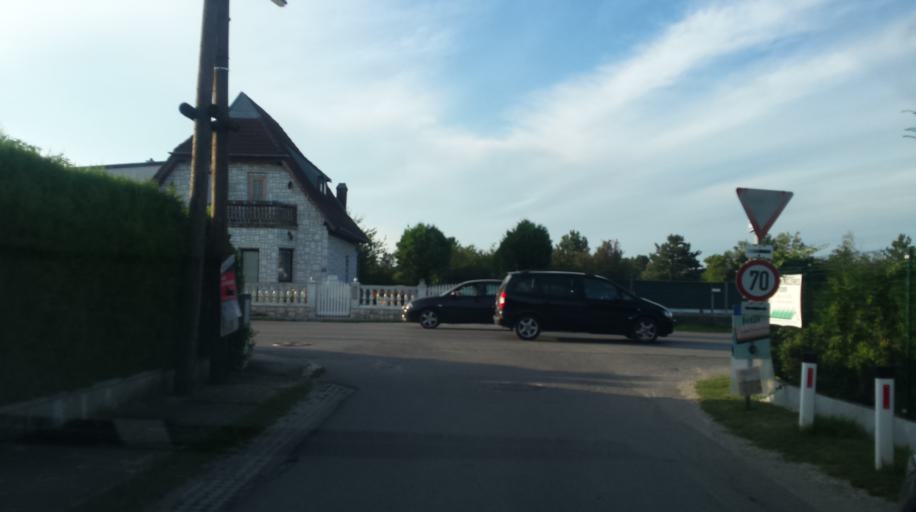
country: AT
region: Lower Austria
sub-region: Politischer Bezirk Ganserndorf
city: Parbasdorf
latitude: 48.3140
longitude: 16.6245
